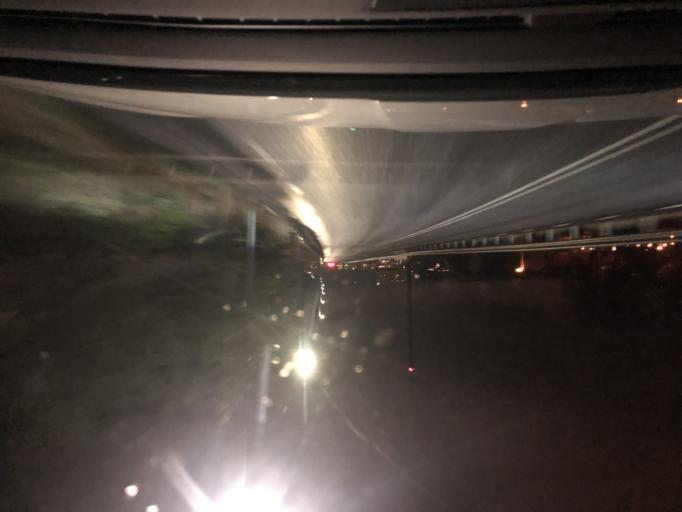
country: SE
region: Stockholm
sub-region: Botkyrka Kommun
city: Tumba
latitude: 59.2002
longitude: 17.8177
